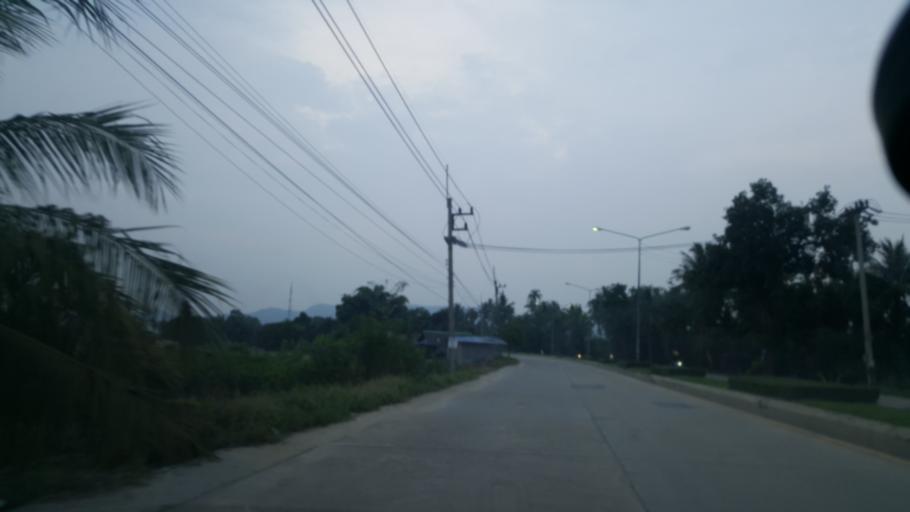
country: TH
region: Chon Buri
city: Si Racha
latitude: 13.2360
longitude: 101.0103
